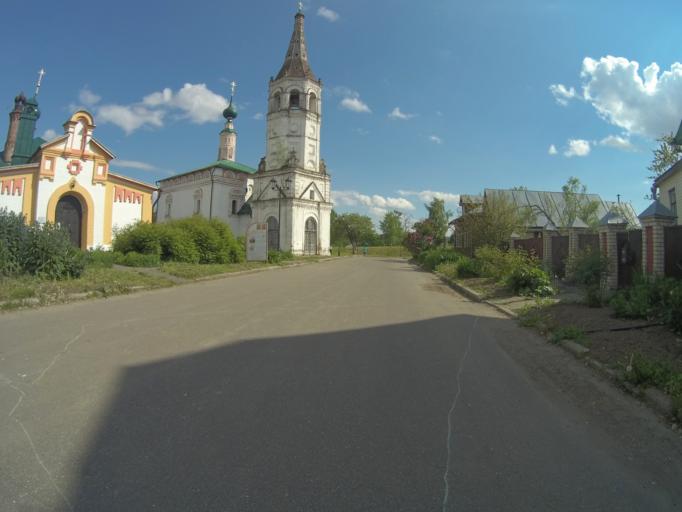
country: RU
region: Vladimir
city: Suzdal'
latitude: 56.4158
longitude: 40.4462
